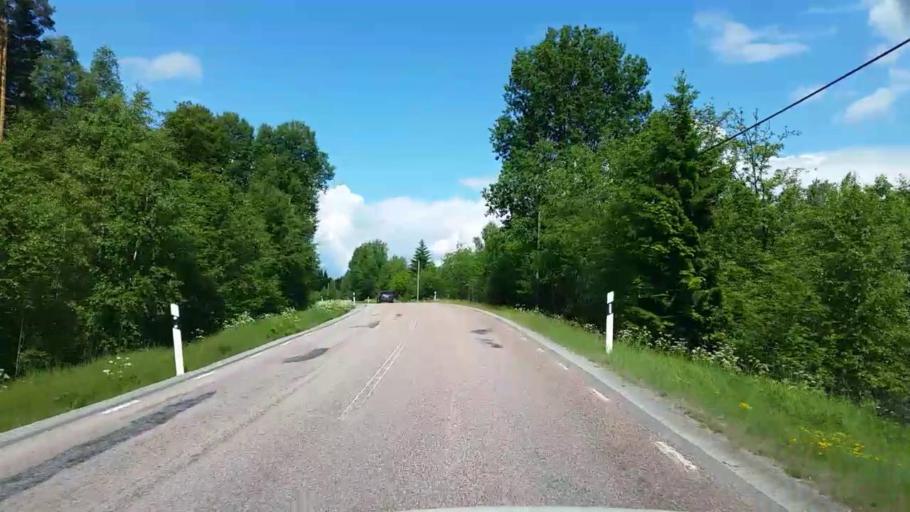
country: SE
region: Vaestmanland
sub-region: Fagersta Kommun
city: Fagersta
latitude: 59.9346
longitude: 15.8246
